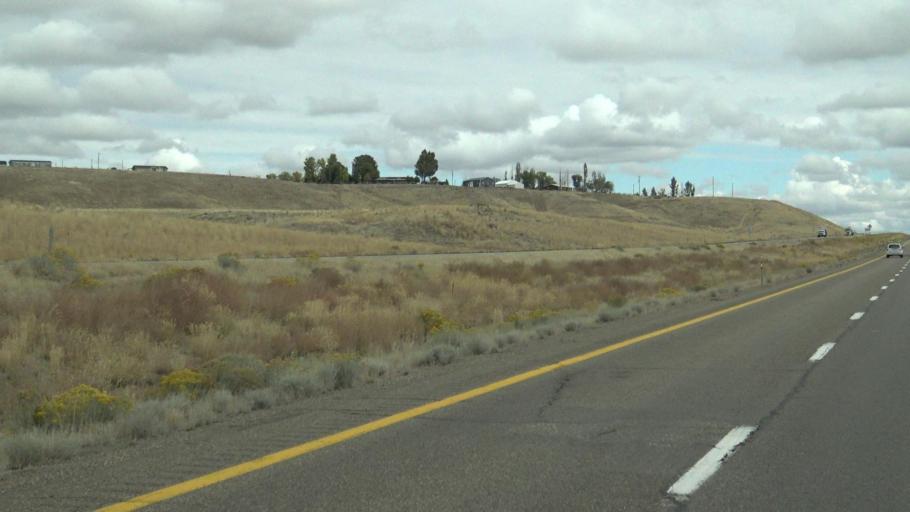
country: US
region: Nevada
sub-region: Elko County
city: Elko
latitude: 40.9226
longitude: -115.6821
